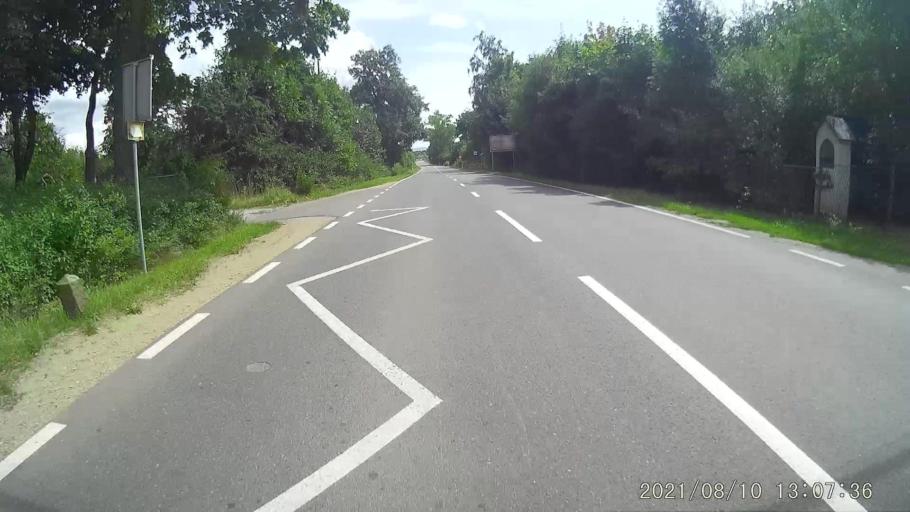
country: PL
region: Lower Silesian Voivodeship
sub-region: Powiat klodzki
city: Bozkow
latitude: 50.4892
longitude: 16.5710
